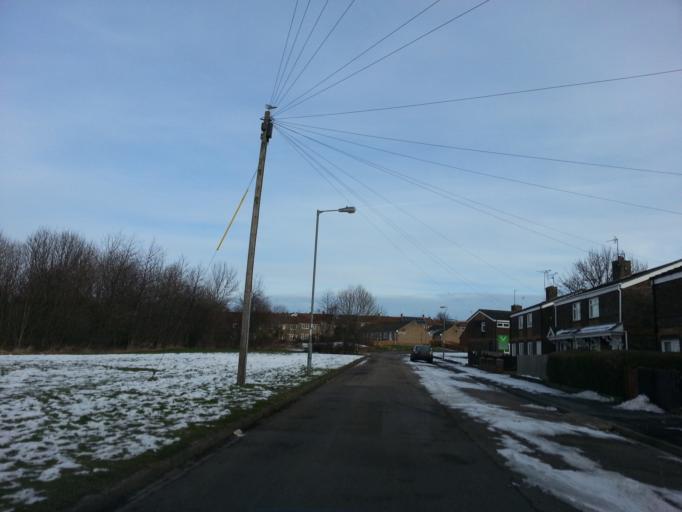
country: GB
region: England
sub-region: County Durham
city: Crook
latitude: 54.7077
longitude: -1.7428
